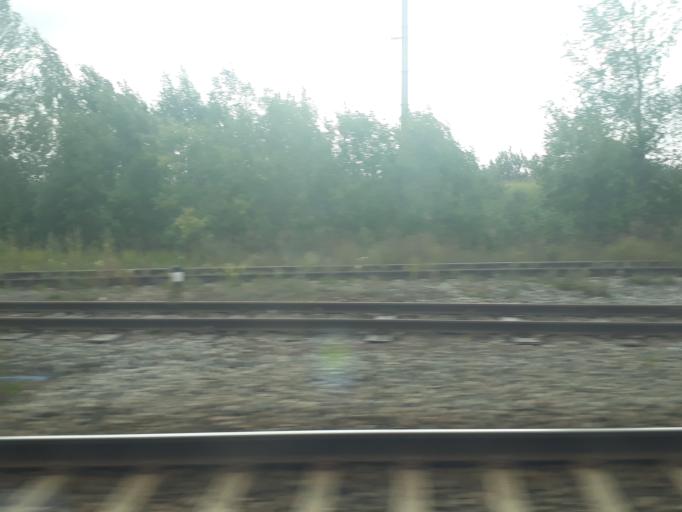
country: EE
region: Laeaene-Virumaa
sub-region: Tapa vald
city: Tapa
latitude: 59.2623
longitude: 25.9213
